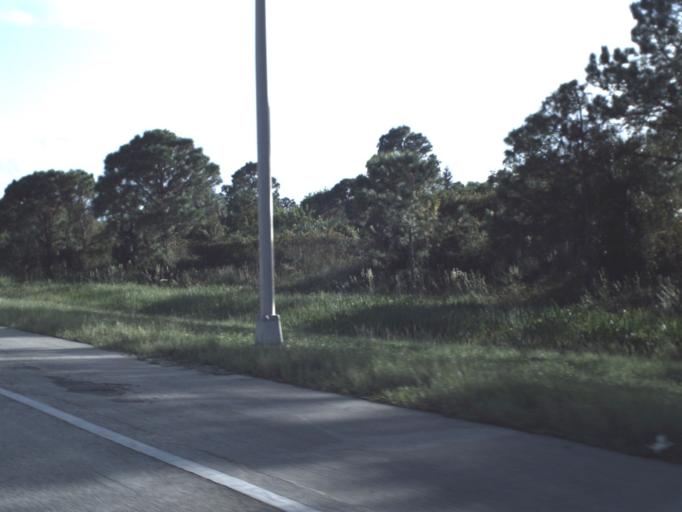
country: US
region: Florida
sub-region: Martin County
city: North River Shores
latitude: 27.2168
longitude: -80.3372
